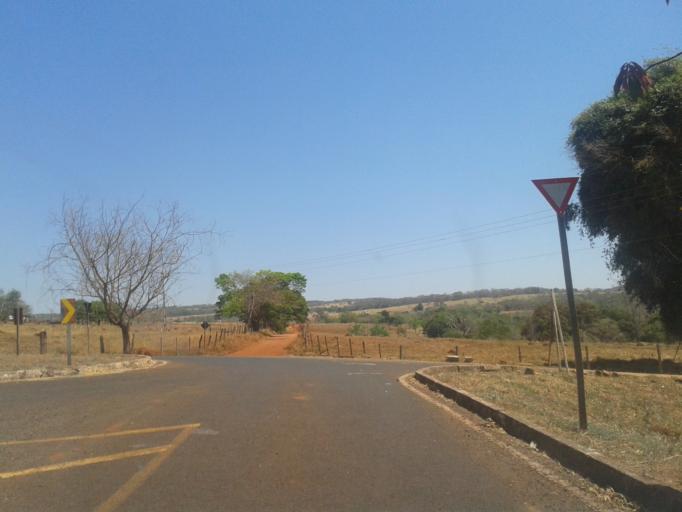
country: BR
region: Minas Gerais
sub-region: Uberlandia
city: Uberlandia
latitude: -18.7716
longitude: -48.2973
